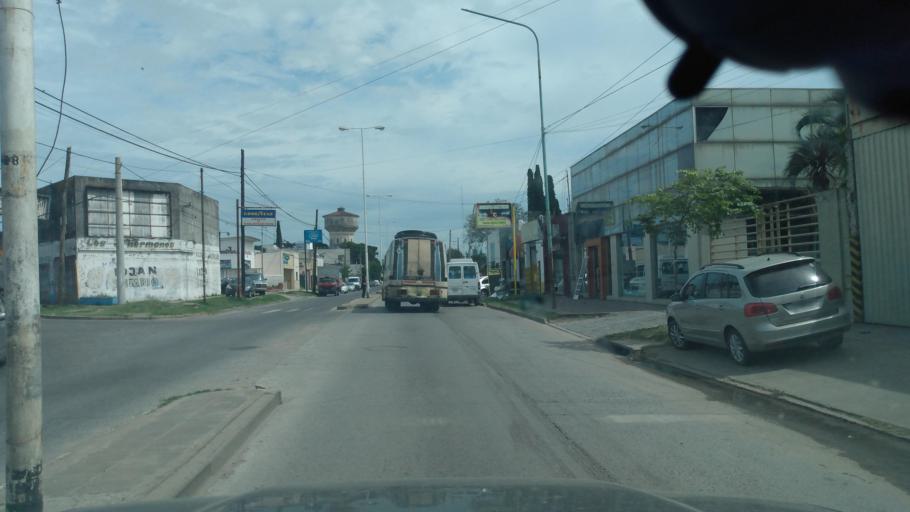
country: AR
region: Buenos Aires
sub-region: Partido de Lujan
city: Lujan
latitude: -34.5744
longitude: -59.0910
